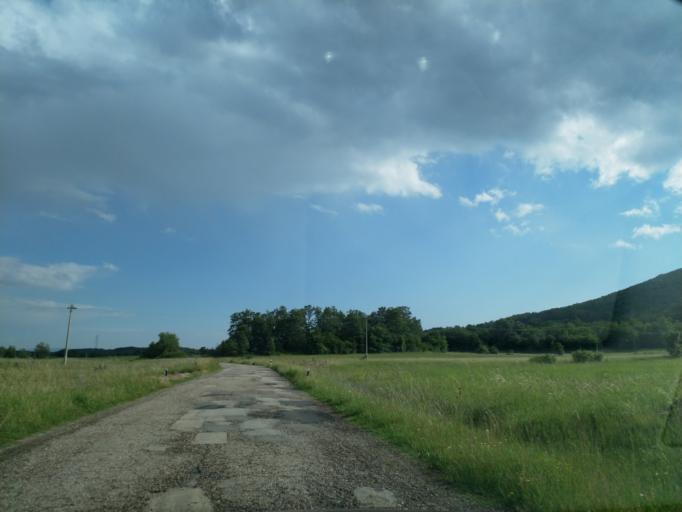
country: RS
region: Central Serbia
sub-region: Borski Okrug
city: Bor
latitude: 43.9869
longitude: 21.9739
